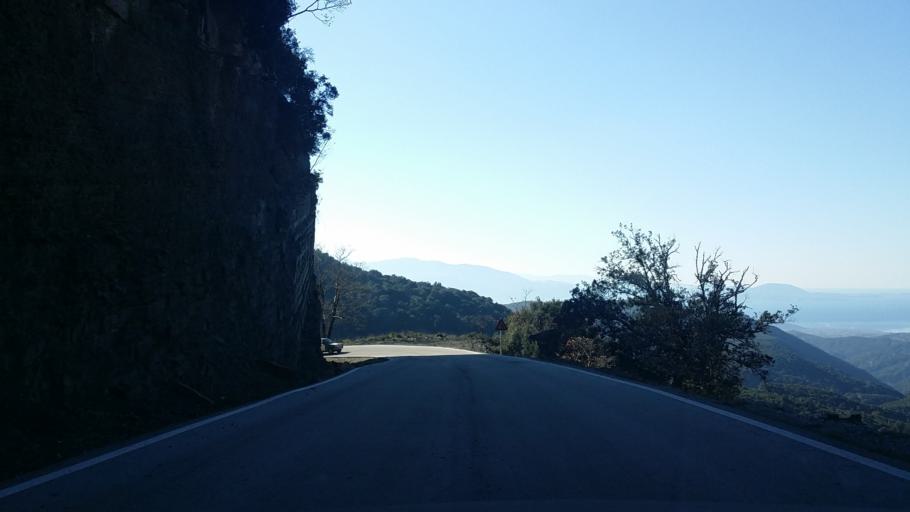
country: GR
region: West Greece
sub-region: Nomos Aitolias kai Akarnanias
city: Krikellos
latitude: 38.9725
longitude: 21.2752
